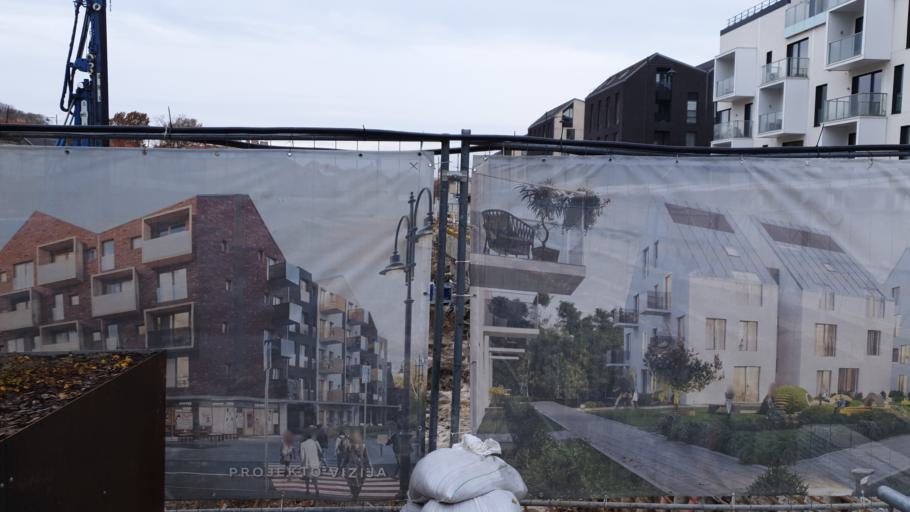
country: LT
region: Vilnius County
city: Rasos
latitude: 54.6790
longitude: 25.3024
